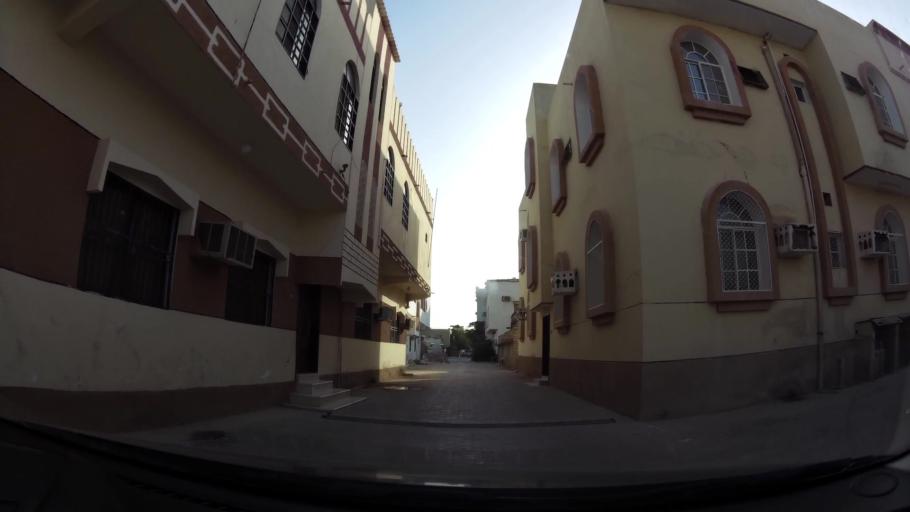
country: OM
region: Zufar
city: Salalah
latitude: 17.0085
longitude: 54.0828
